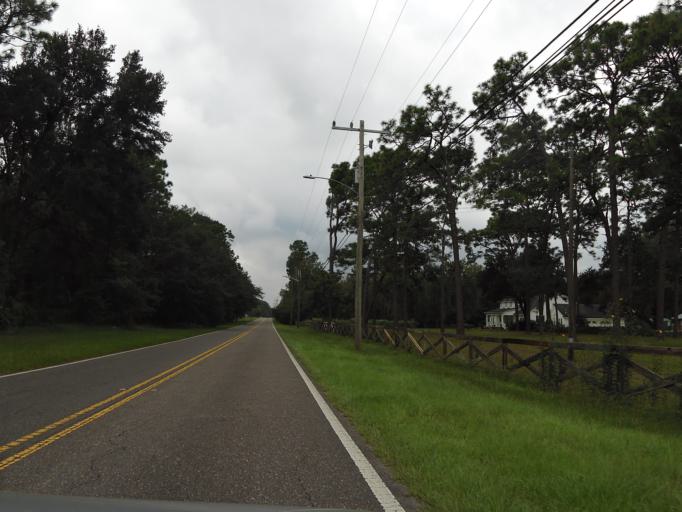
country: US
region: Florida
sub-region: Clay County
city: Bellair-Meadowbrook Terrace
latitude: 30.2235
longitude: -81.7728
